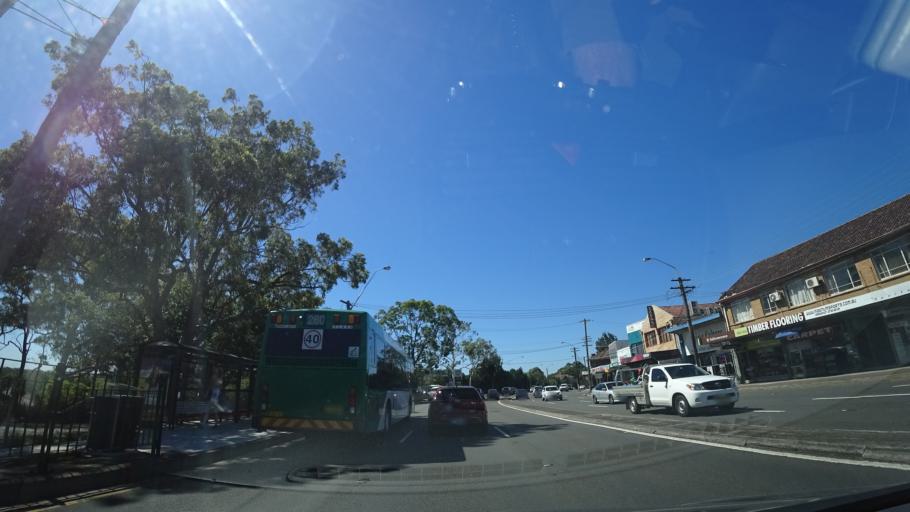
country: AU
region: New South Wales
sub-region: Ku-ring-gai
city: Roseville Chase
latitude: -33.7788
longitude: 151.1951
